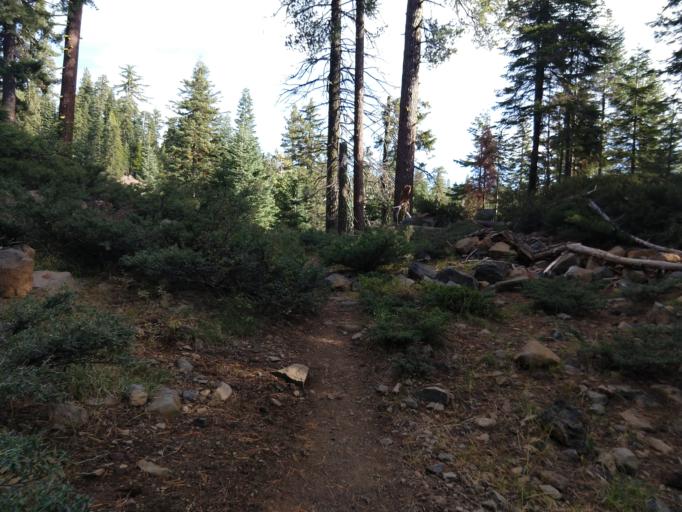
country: US
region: California
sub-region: Plumas County
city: Chester
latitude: 40.4197
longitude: -121.3766
